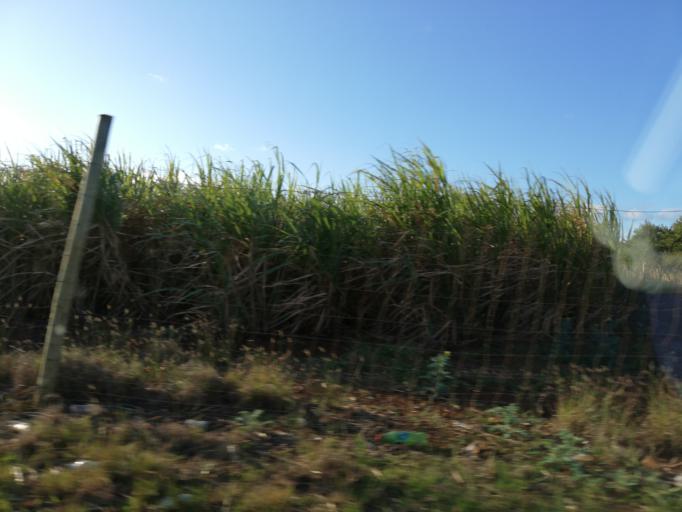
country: MU
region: Pamplemousses
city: Arsenal
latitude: -20.0802
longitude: 57.5329
